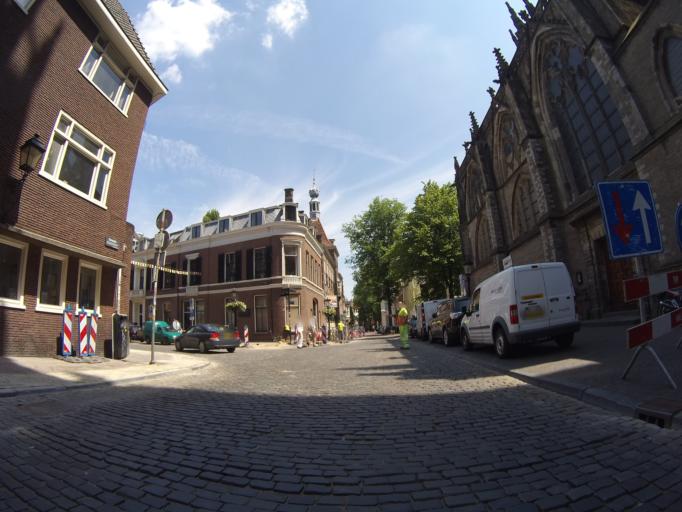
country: NL
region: Utrecht
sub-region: Gemeente Utrecht
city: Utrecht
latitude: 52.0911
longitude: 5.1222
